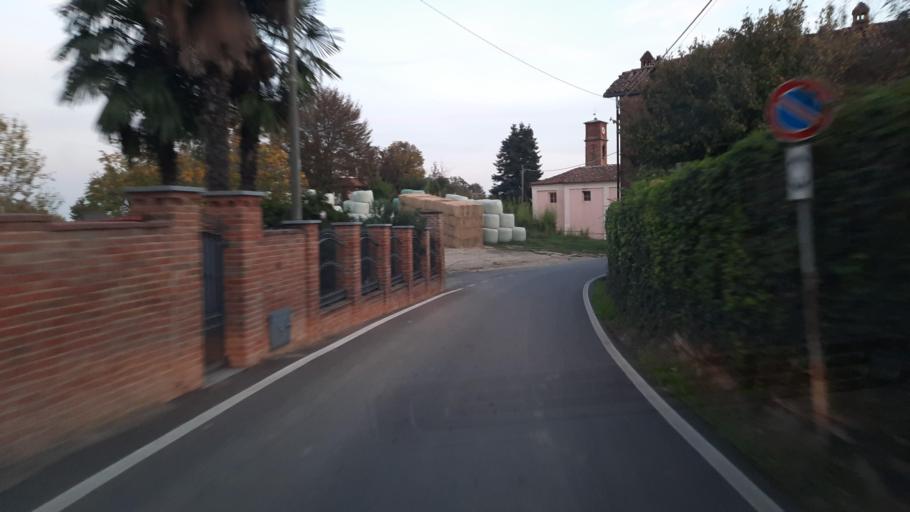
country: IT
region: Piedmont
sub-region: Provincia di Asti
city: Tonco
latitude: 45.0247
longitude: 8.1949
